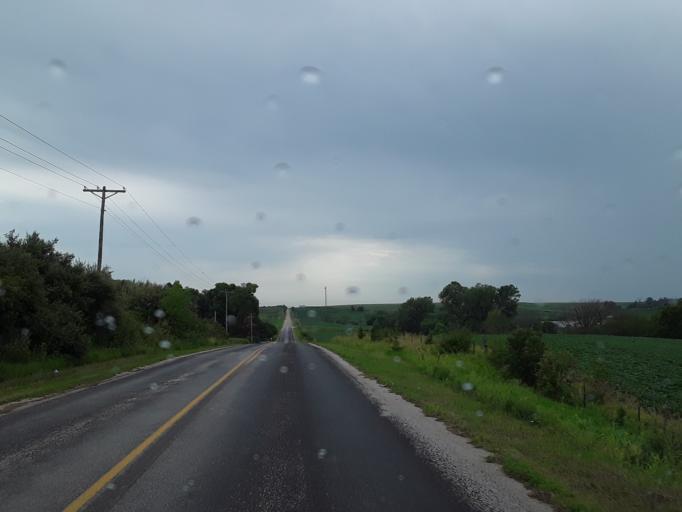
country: US
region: Nebraska
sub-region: Washington County
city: Blair
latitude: 41.5092
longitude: -96.1608
